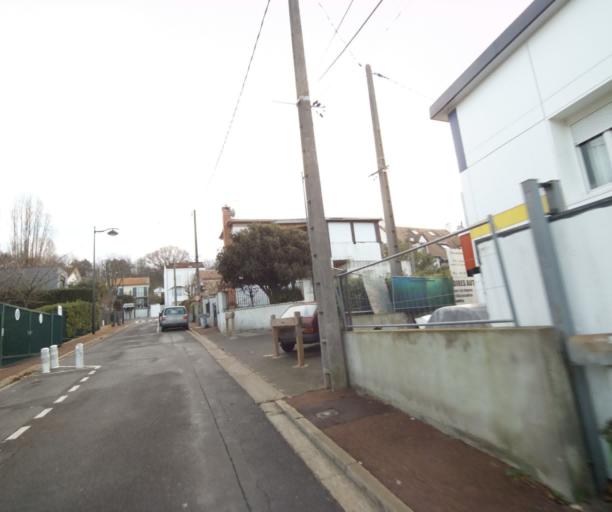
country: FR
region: Ile-de-France
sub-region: Departement des Hauts-de-Seine
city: Rueil-Malmaison
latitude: 48.8751
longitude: 2.2047
